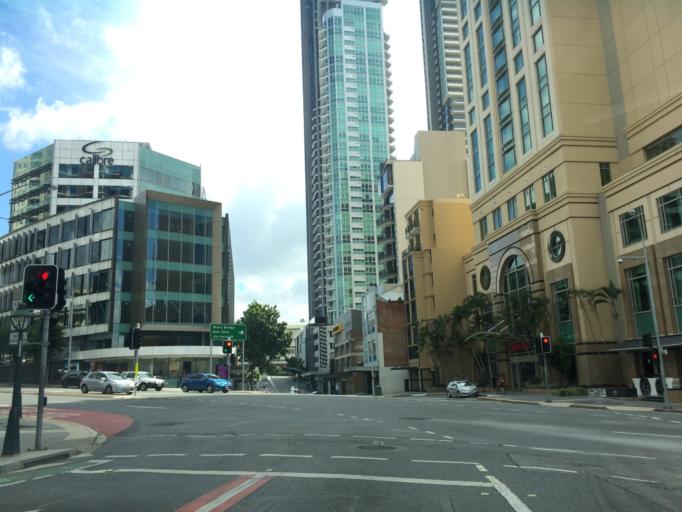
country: AU
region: Queensland
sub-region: Brisbane
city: Brisbane
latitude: -27.4638
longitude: 153.0310
